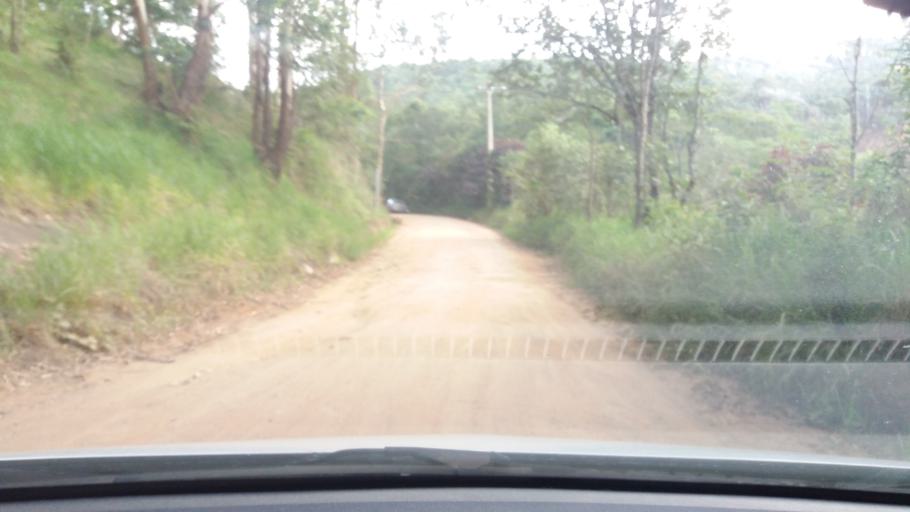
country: BR
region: Sao Paulo
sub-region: Bom Jesus Dos Perdoes
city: Bom Jesus dos Perdoes
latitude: -23.1861
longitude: -46.4858
